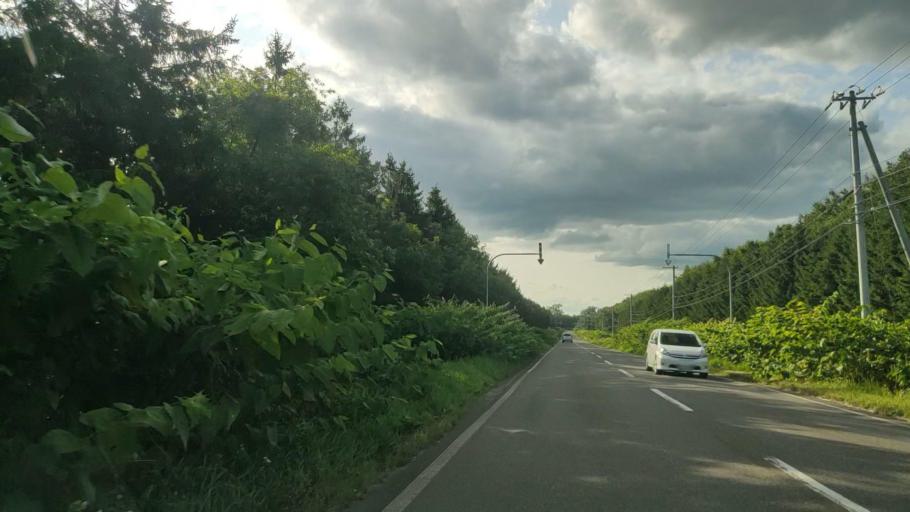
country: JP
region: Hokkaido
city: Makubetsu
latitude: 44.9017
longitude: 141.9097
